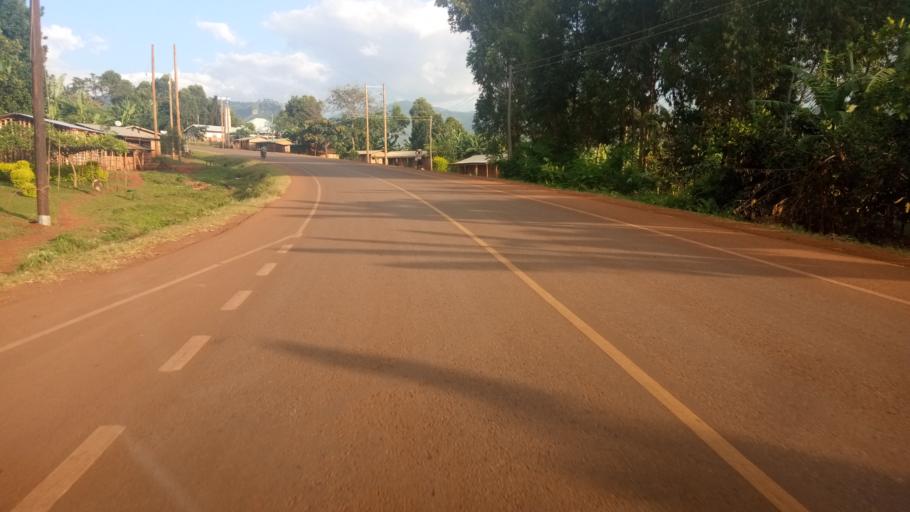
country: UG
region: Eastern Region
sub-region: Sironko District
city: Sironko
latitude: 1.3196
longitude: 34.3387
